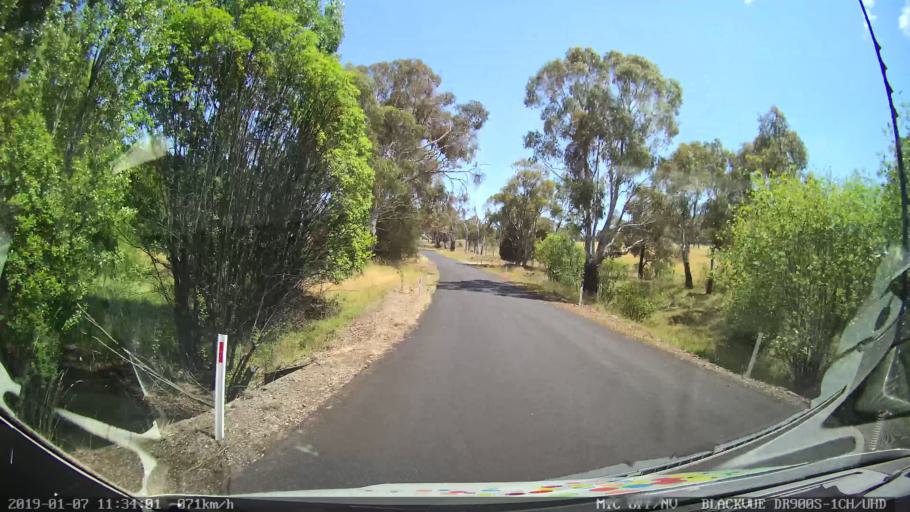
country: AU
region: New South Wales
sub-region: Armidale Dumaresq
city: Armidale
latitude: -30.3939
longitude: 151.5604
